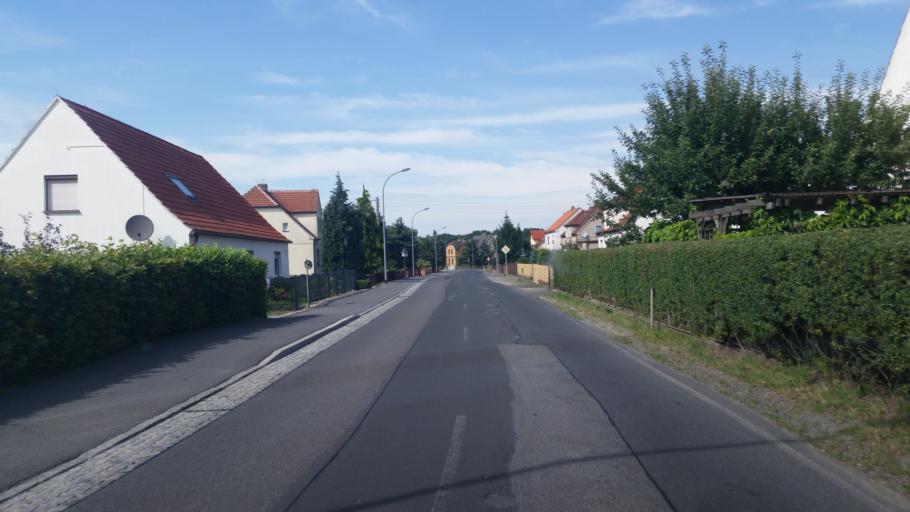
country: DE
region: Saxony
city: Bernsdorf
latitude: 51.3552
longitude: 14.0674
